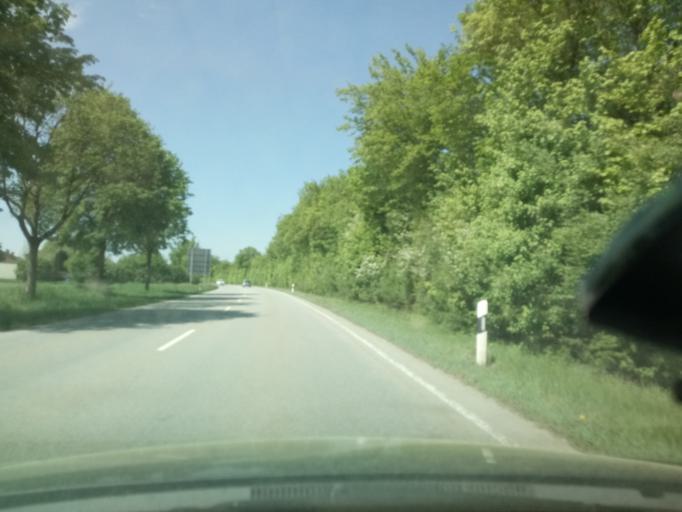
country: DE
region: Bavaria
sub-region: Upper Bavaria
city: Altoetting
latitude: 48.2364
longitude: 12.6749
